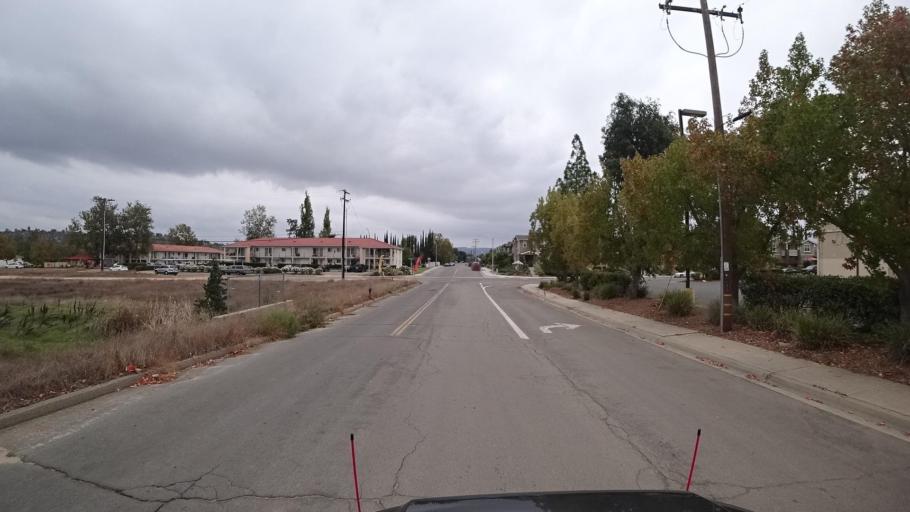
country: US
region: California
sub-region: San Diego County
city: Ramona
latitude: 33.0363
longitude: -116.8827
